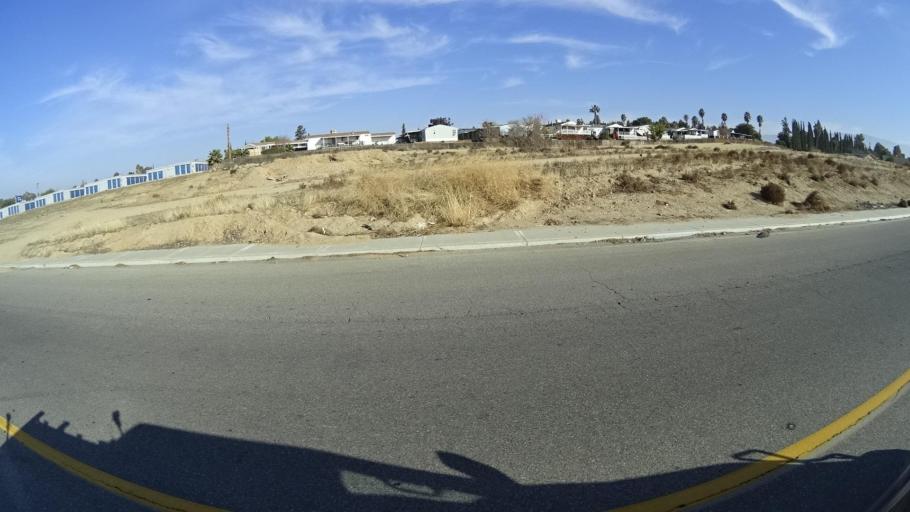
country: US
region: California
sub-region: Kern County
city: Bakersfield
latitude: 35.3756
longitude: -118.9074
